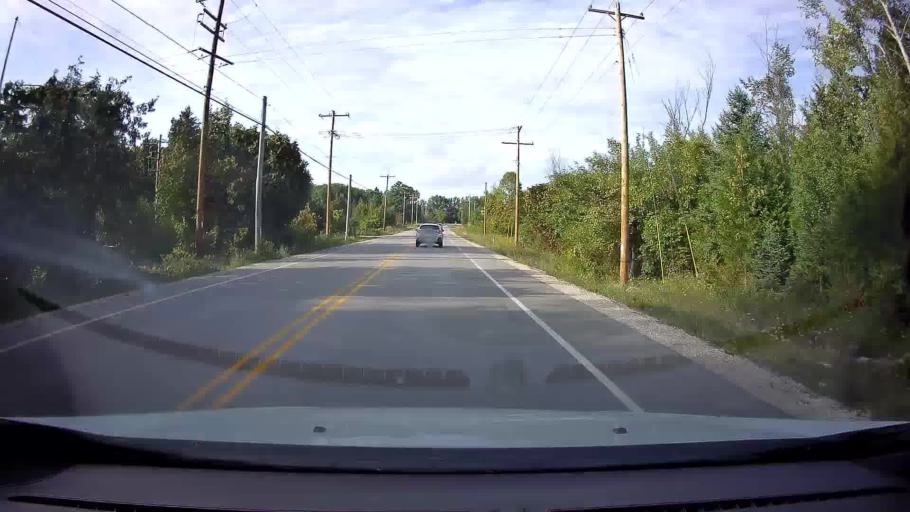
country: US
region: Wisconsin
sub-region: Door County
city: Sturgeon Bay
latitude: 45.1672
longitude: -87.1325
